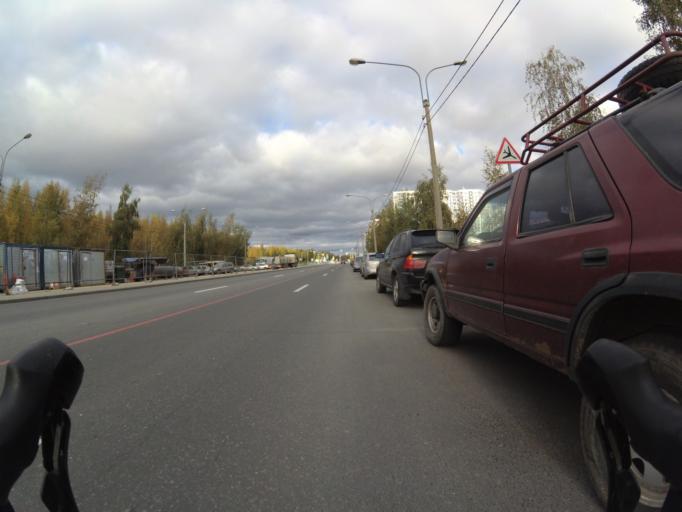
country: RU
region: Leningrad
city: Untolovo
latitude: 60.0014
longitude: 30.1946
